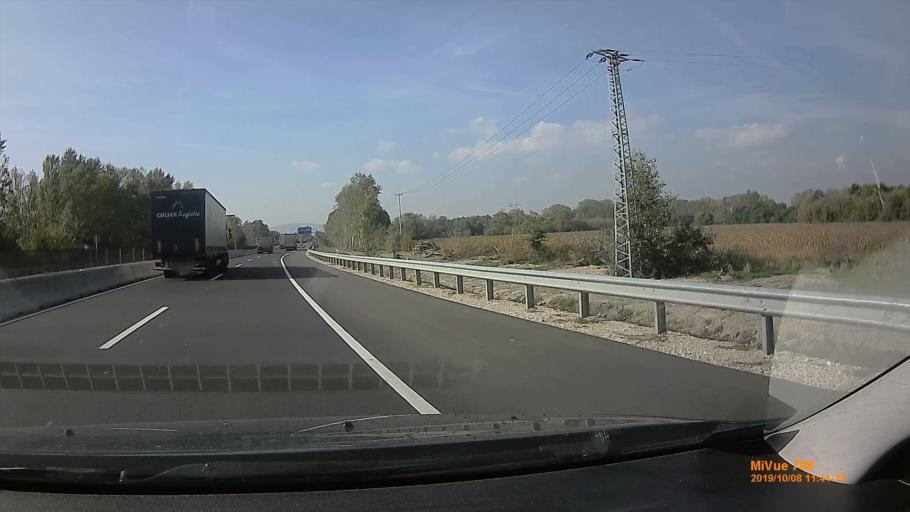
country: HU
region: Pest
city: Dunakeszi
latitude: 47.5990
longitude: 19.1457
